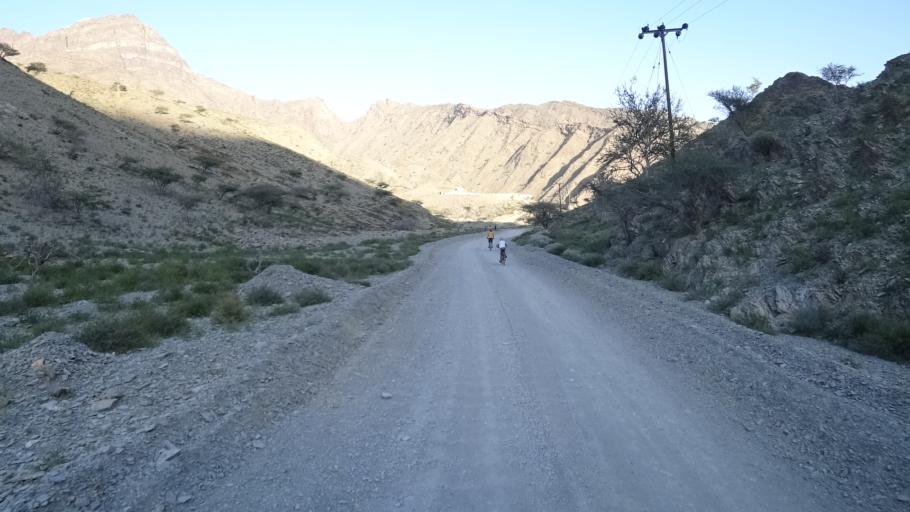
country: OM
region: Al Batinah
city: Rustaq
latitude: 23.2674
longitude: 57.3933
